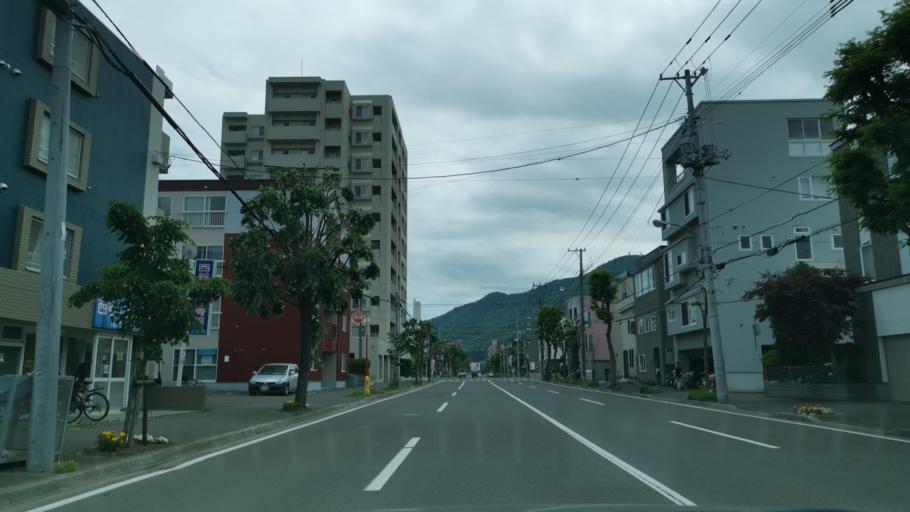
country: JP
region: Hokkaido
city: Sapporo
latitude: 43.0454
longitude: 141.3324
